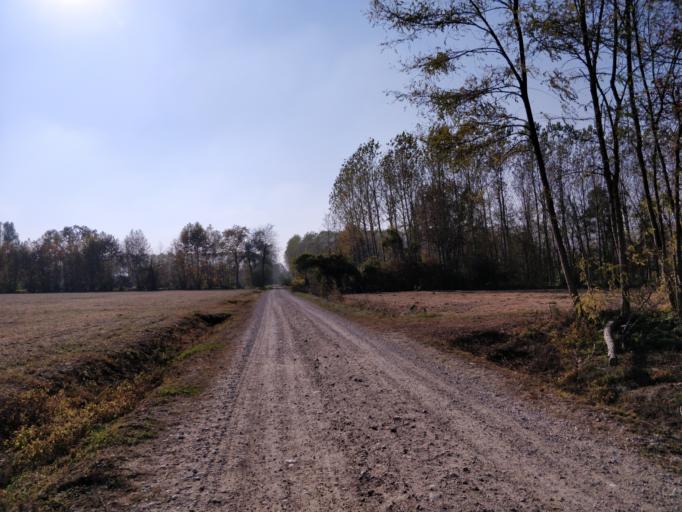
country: IT
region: Friuli Venezia Giulia
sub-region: Provincia di Udine
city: Bertiolo
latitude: 45.9288
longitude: 13.0384
